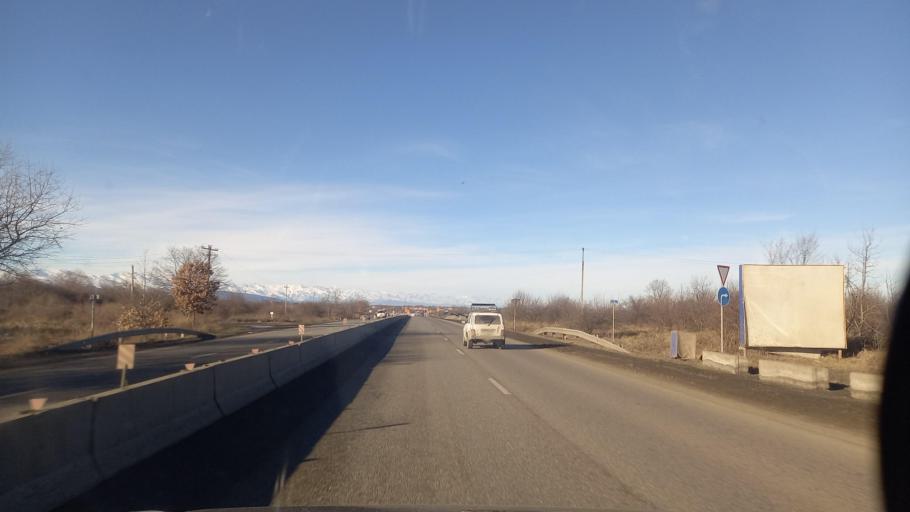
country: RU
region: North Ossetia
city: Gizel'
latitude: 43.0268
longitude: 44.6139
